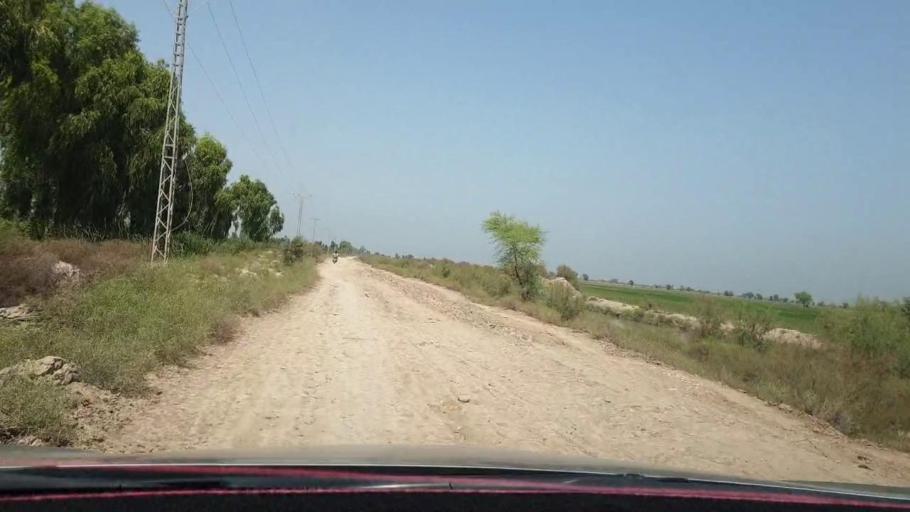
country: PK
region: Sindh
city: Warah
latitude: 27.4170
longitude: 67.6983
